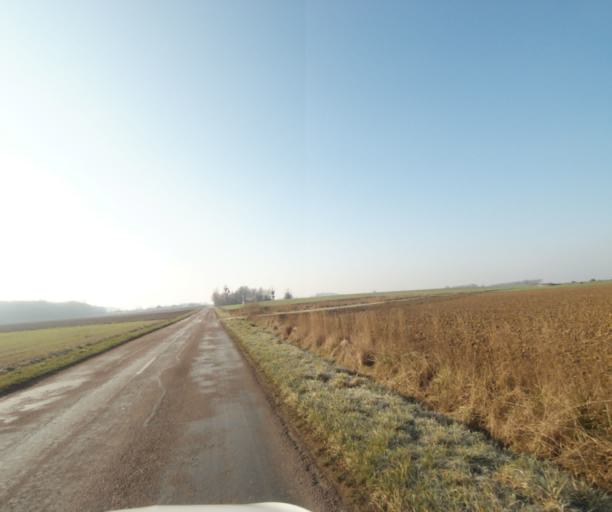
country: FR
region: Champagne-Ardenne
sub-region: Departement de la Haute-Marne
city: Montier-en-Der
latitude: 48.4476
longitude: 4.7627
